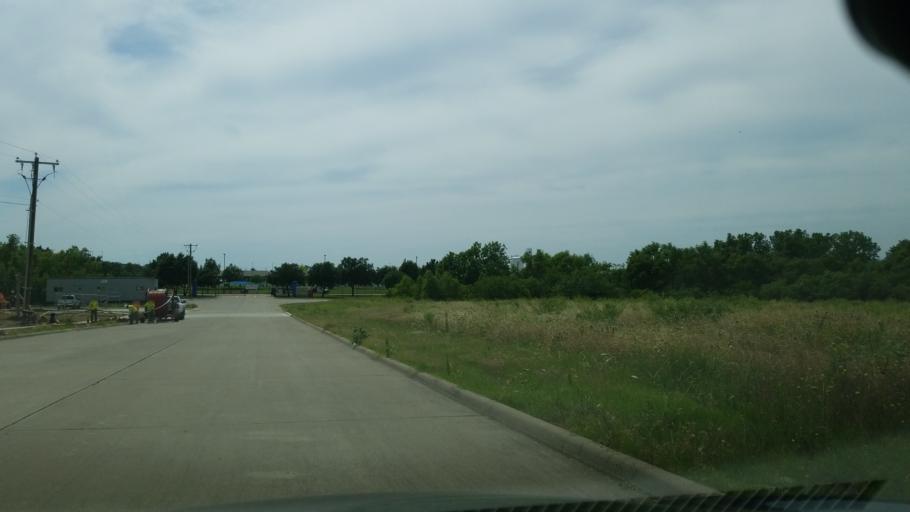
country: US
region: Texas
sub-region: Dallas County
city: Coppell
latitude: 32.8814
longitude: -96.9924
